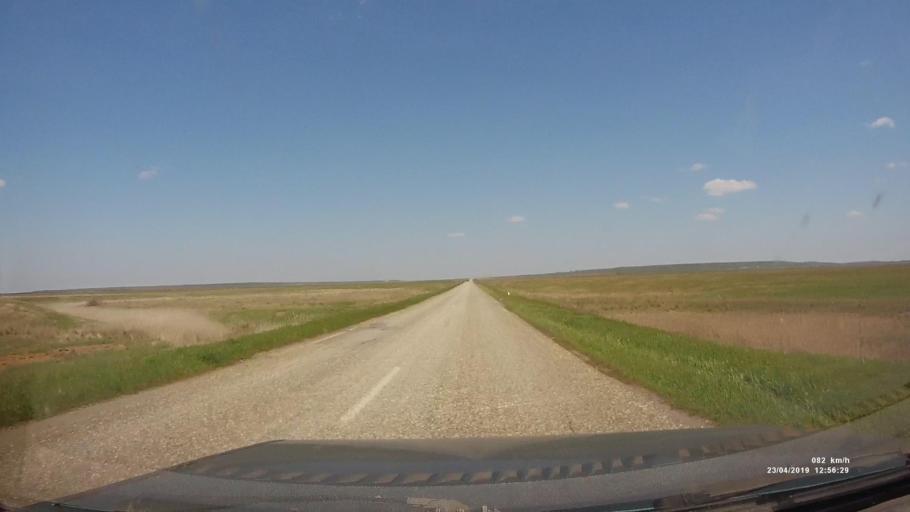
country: RU
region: Kalmykiya
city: Yashalta
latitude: 46.5944
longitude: 42.5719
